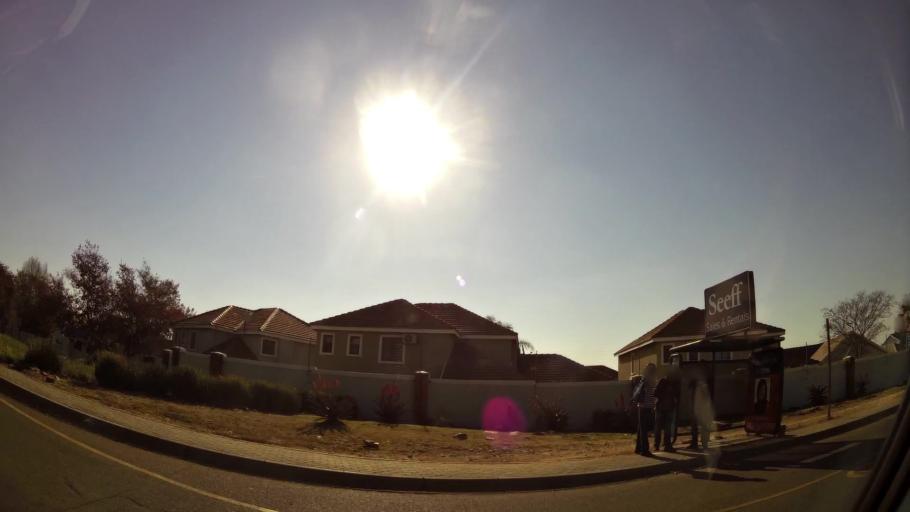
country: ZA
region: Gauteng
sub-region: City of Tshwane Metropolitan Municipality
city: Centurion
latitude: -25.8252
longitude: 28.3073
